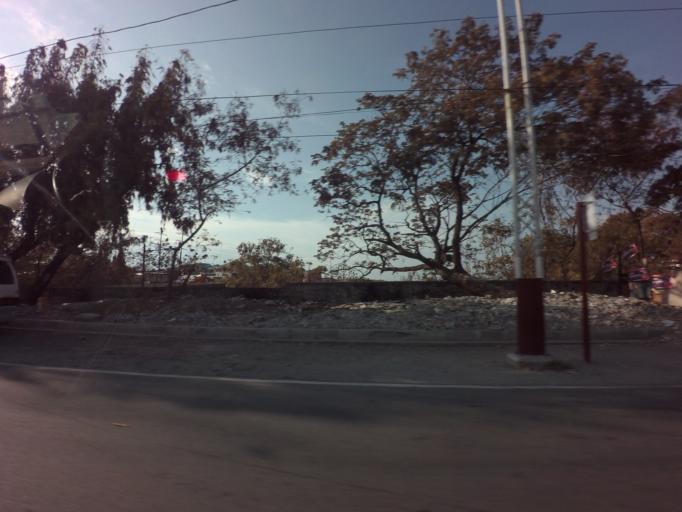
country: PH
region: Calabarzon
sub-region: Province of Rizal
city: Taguig
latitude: 14.4889
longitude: 121.0565
